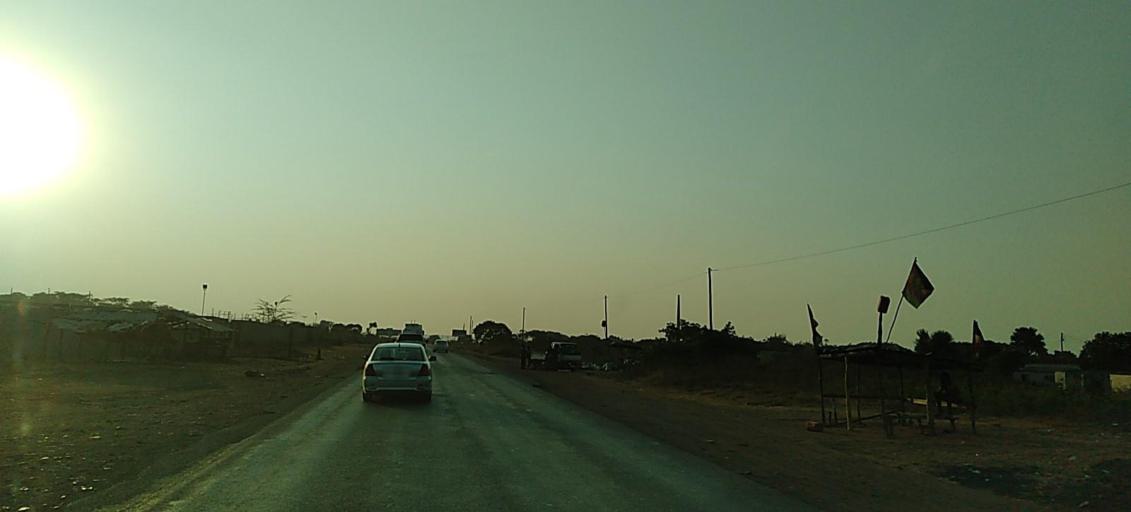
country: ZM
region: Copperbelt
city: Ndola
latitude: -13.0306
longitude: 28.6843
